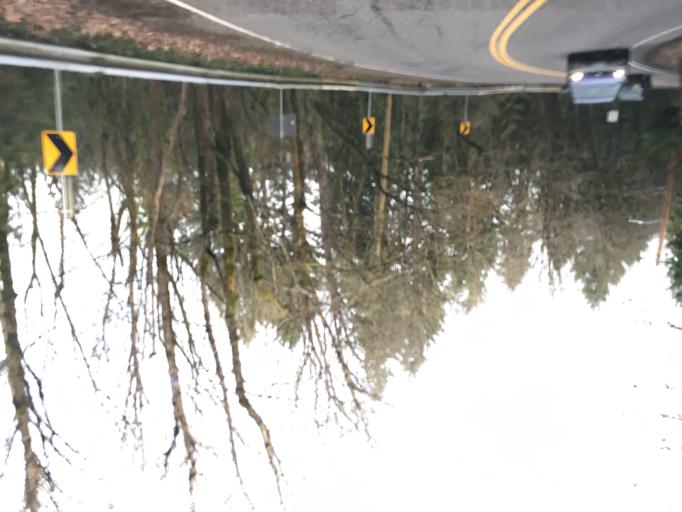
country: US
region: Oregon
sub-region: Clackamas County
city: Lake Oswego
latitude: 45.4404
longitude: -122.6855
